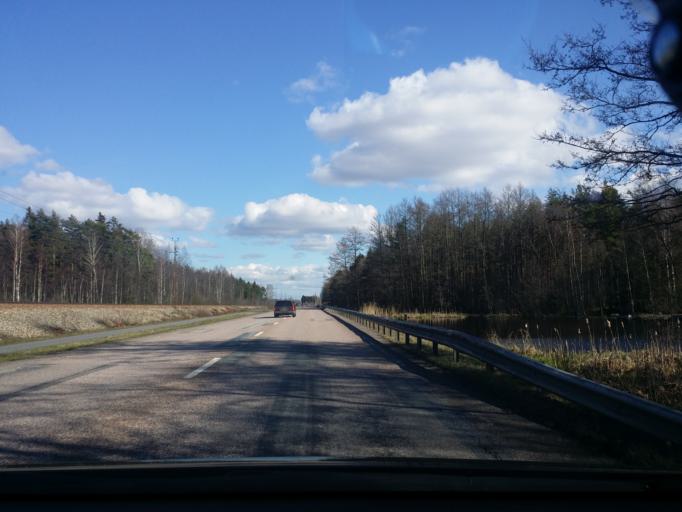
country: SE
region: Vaestmanland
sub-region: Sala Kommun
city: Sala
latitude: 59.9394
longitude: 16.5590
